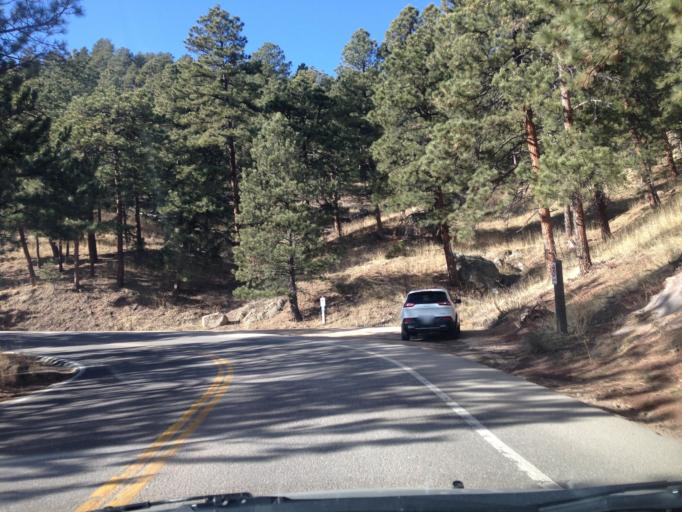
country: US
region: Colorado
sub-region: Boulder County
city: Boulder
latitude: 40.0019
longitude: -105.2976
